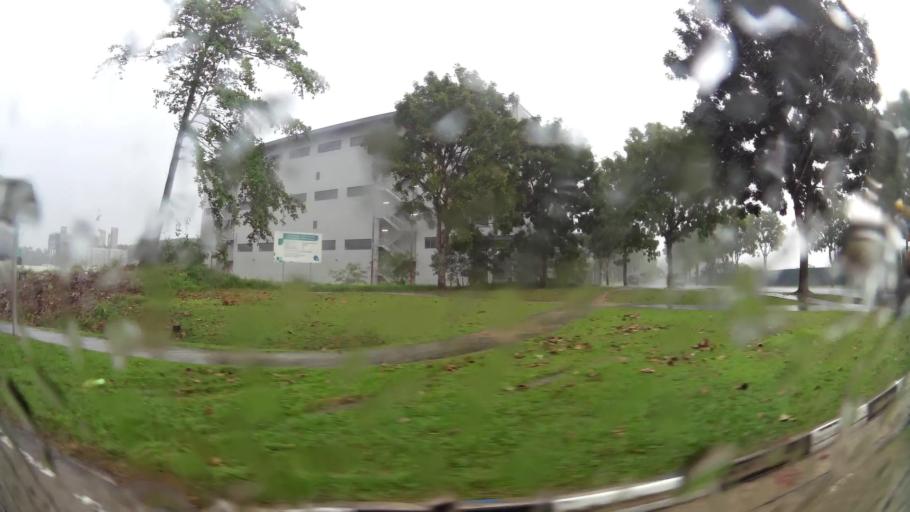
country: MY
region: Johor
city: Kampung Pasir Gudang Baru
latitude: 1.3756
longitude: 103.9201
